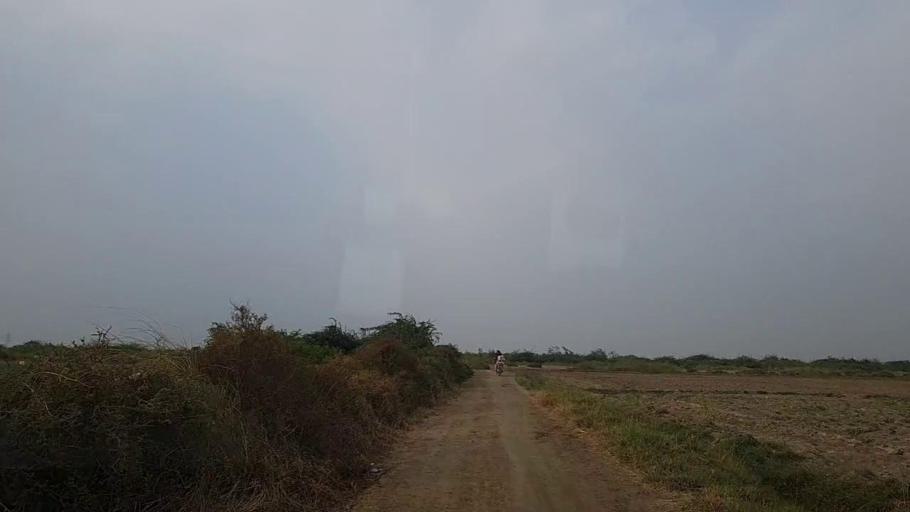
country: PK
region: Sindh
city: Mirpur Sakro
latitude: 24.6193
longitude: 67.5039
